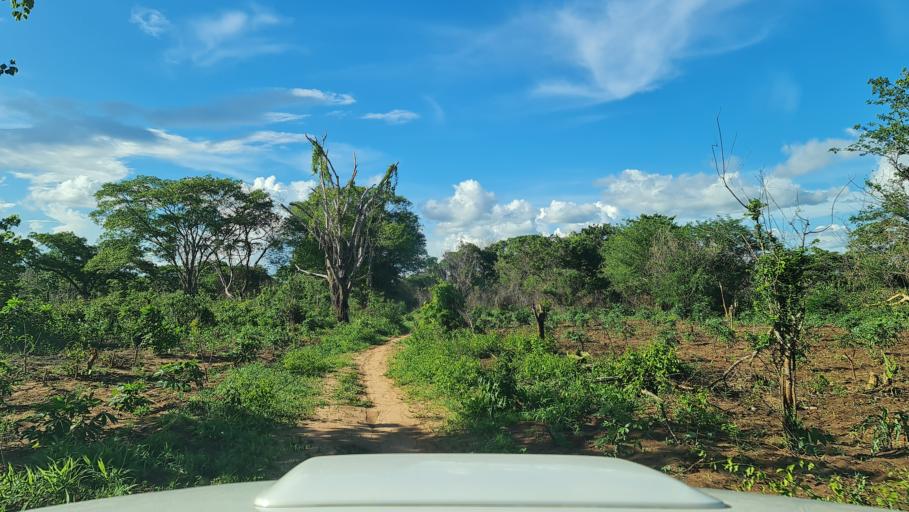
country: MZ
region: Nampula
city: Ilha de Mocambique
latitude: -15.2498
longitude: 40.1807
